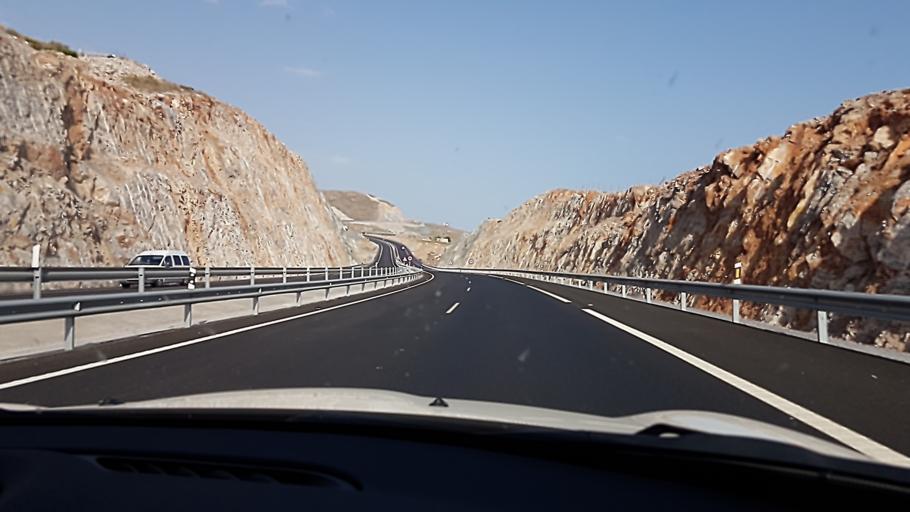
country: ES
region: Andalusia
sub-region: Provincia de Granada
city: Gualchos
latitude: 36.7098
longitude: -3.4094
